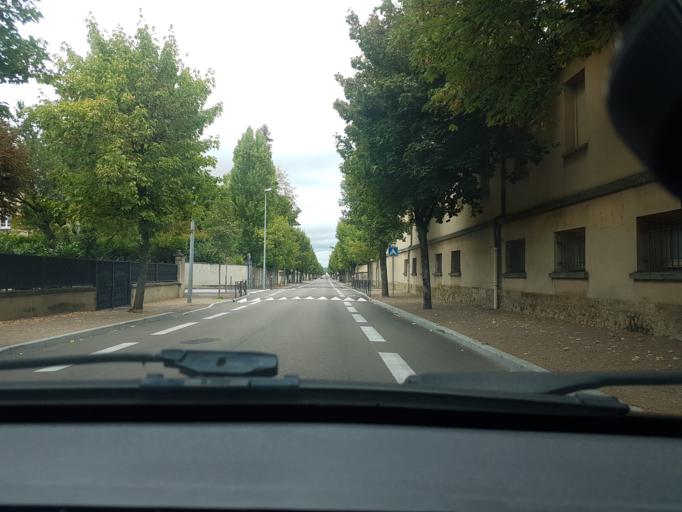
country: FR
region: Bourgogne
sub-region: Departement de l'Yonne
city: Auxerre
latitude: 47.7989
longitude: 3.5615
